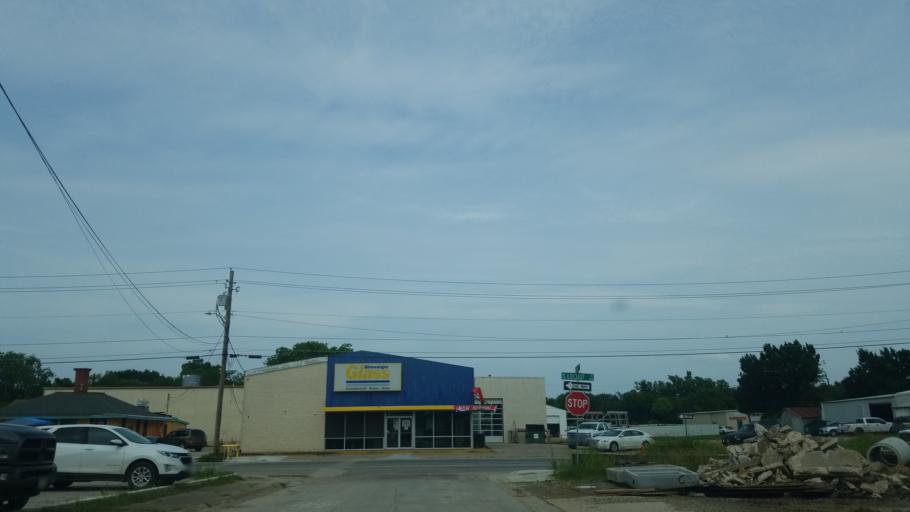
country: US
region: Texas
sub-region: Denton County
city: Denton
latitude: 33.2082
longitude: -97.1329
